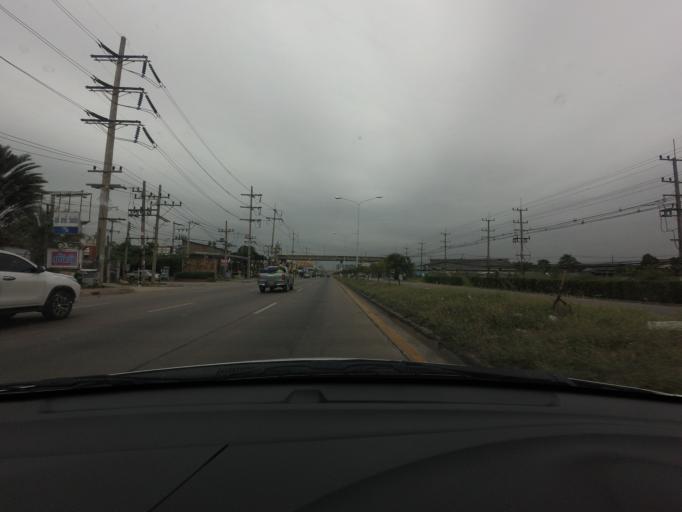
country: TH
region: Nakhon Pathom
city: Sam Phran
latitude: 13.7291
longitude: 100.2499
